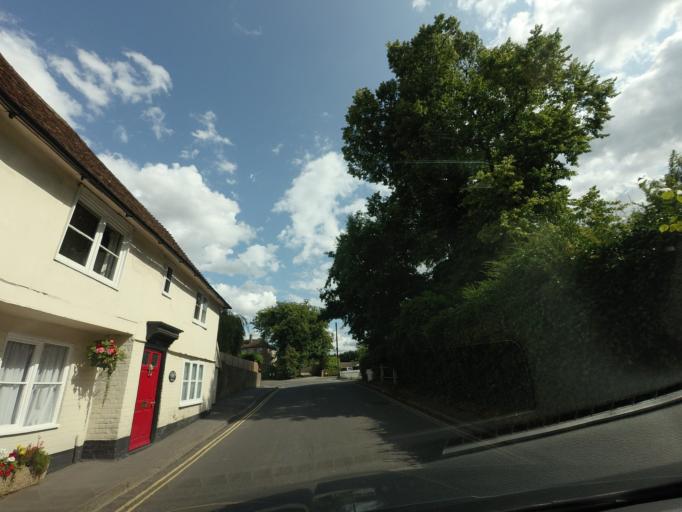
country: GB
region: England
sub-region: Kent
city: Harrietsham
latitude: 51.2613
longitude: 0.6281
